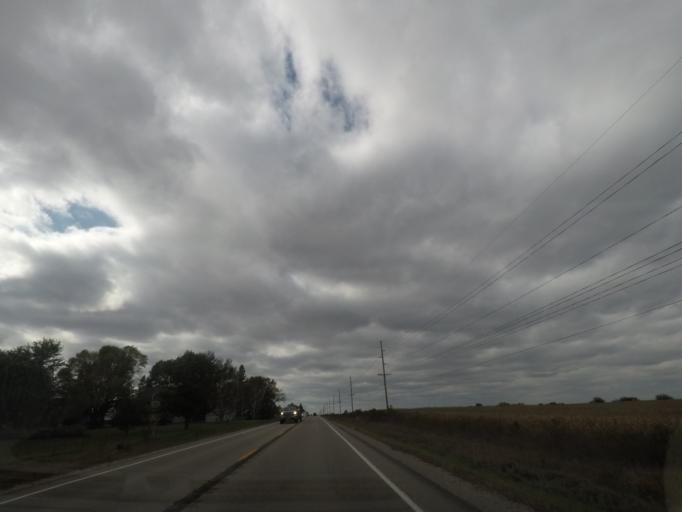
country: US
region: Iowa
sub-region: Story County
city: Huxley
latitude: 41.8778
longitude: -93.5489
